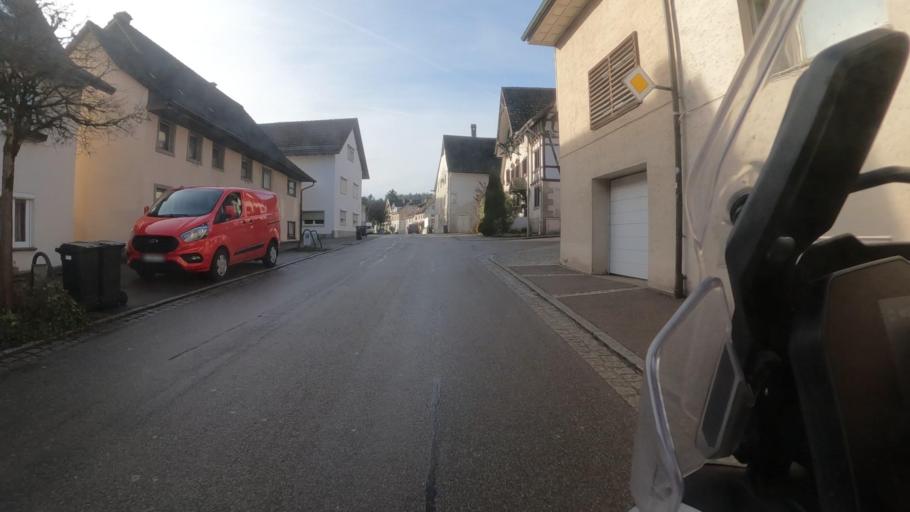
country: DE
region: Baden-Wuerttemberg
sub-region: Freiburg Region
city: Lottstetten
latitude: 47.6267
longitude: 8.5716
